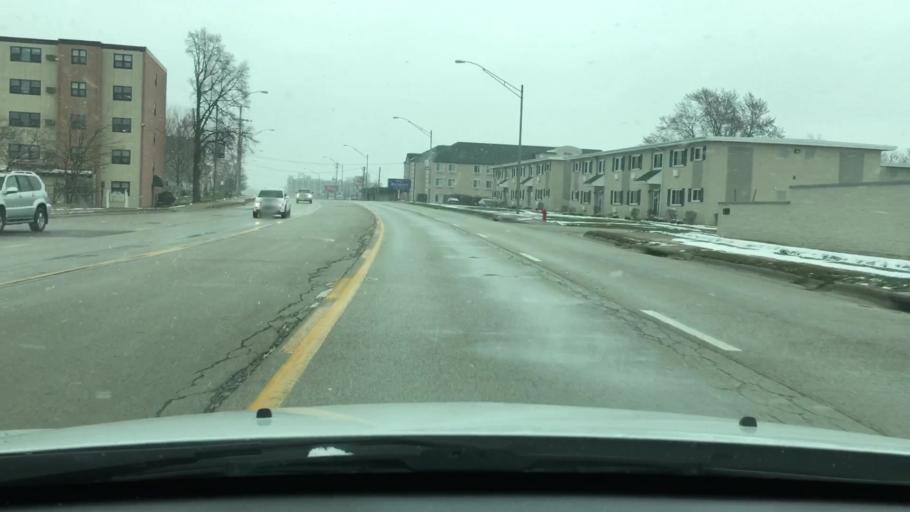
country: US
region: Illinois
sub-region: DeKalb County
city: DeKalb
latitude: 41.9307
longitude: -88.7809
